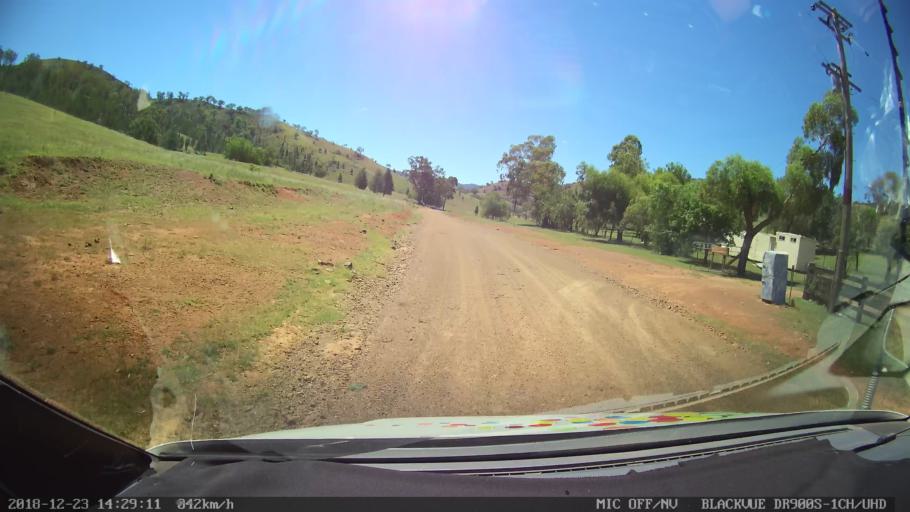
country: AU
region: New South Wales
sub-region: Tamworth Municipality
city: Manilla
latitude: -30.6101
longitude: 150.9388
